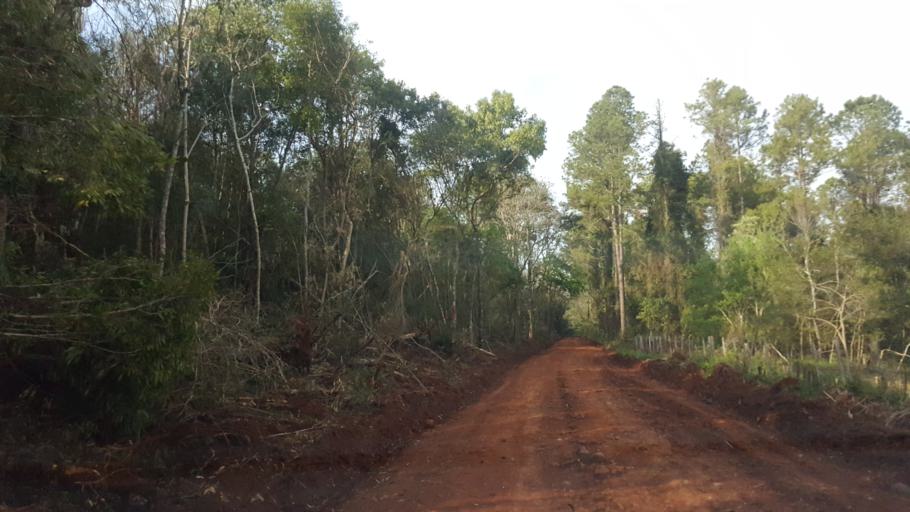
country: AR
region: Misiones
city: Capiovi
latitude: -26.8980
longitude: -55.1071
